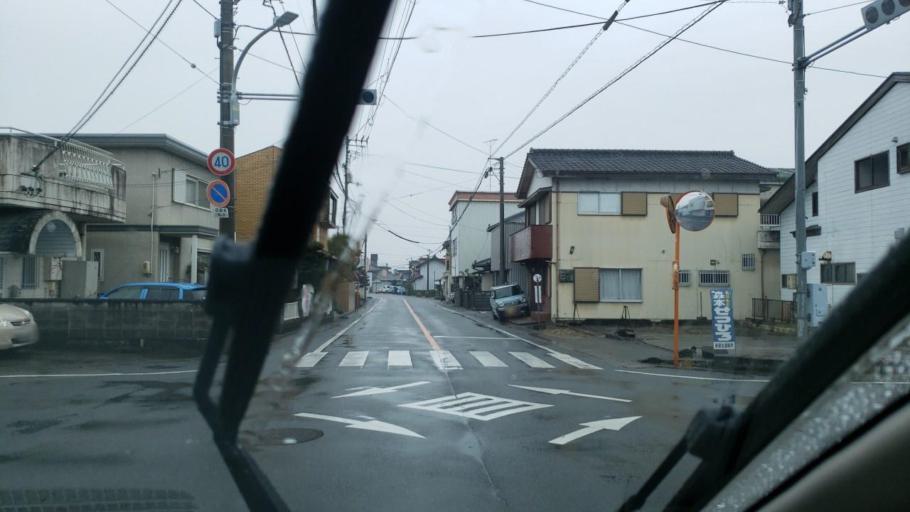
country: JP
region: Tokushima
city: Kamojimacho-jogejima
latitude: 34.0993
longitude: 134.3815
